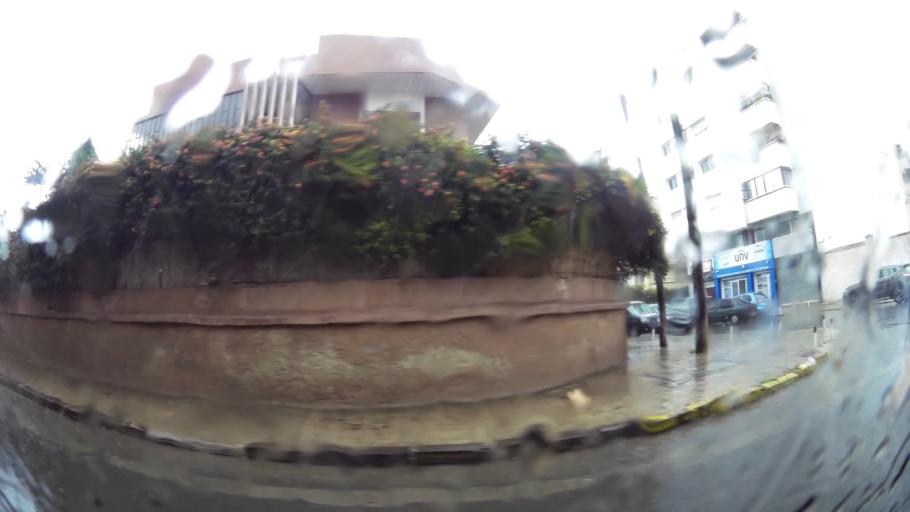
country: MA
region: Grand Casablanca
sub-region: Casablanca
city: Casablanca
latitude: 33.5731
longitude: -7.6282
